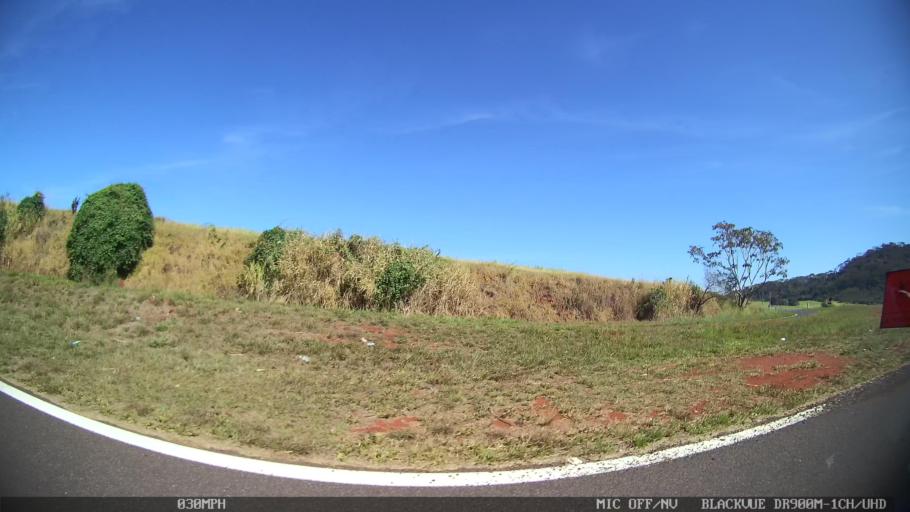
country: BR
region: Sao Paulo
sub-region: Sao Simao
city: Sao Simao
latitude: -21.5292
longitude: -47.6439
